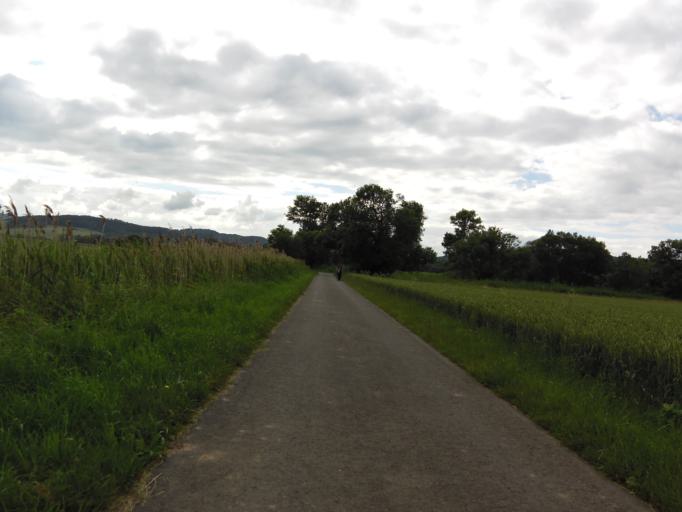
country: DE
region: Thuringia
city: Creuzburg
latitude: 51.0455
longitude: 10.2441
